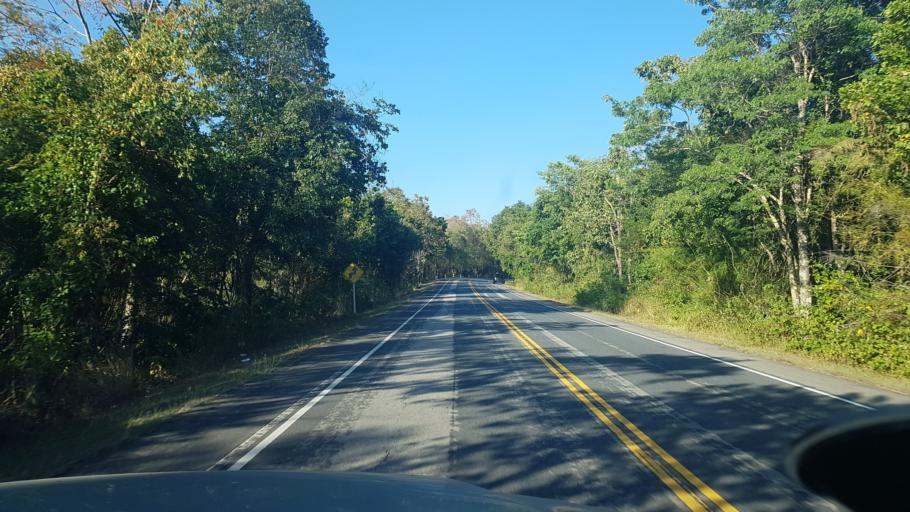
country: TH
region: Phetchabun
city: Lom Sak
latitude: 16.7367
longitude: 101.4224
